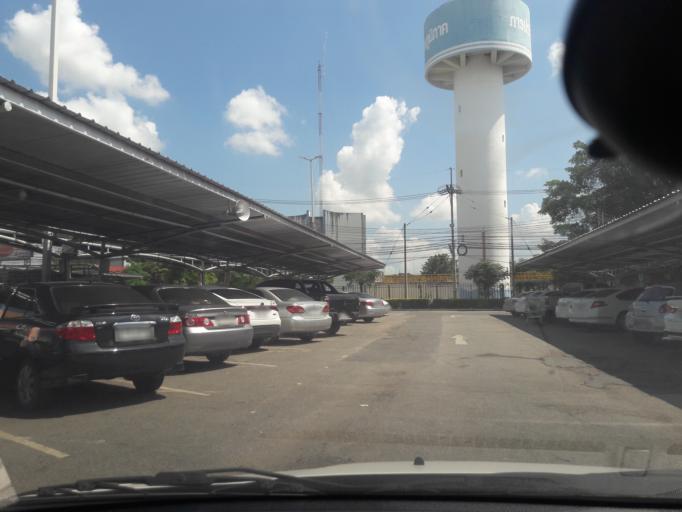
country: TH
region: Chiang Mai
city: Chiang Mai
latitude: 18.8093
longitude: 98.9973
